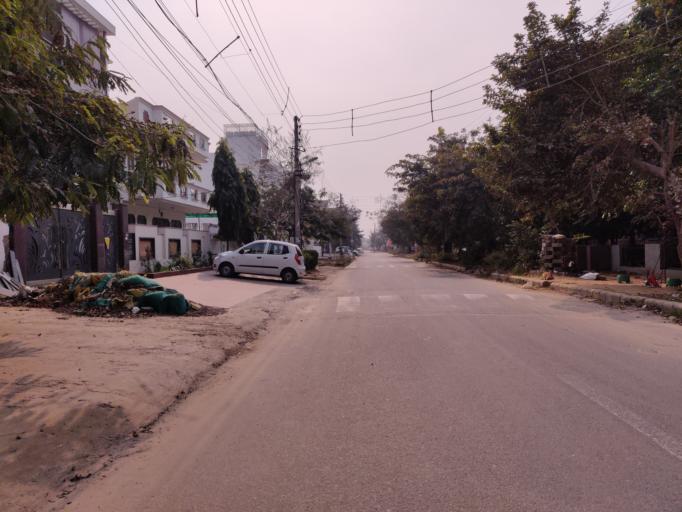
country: IN
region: Haryana
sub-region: Gurgaon
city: Gurgaon
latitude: 28.4416
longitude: 77.0688
